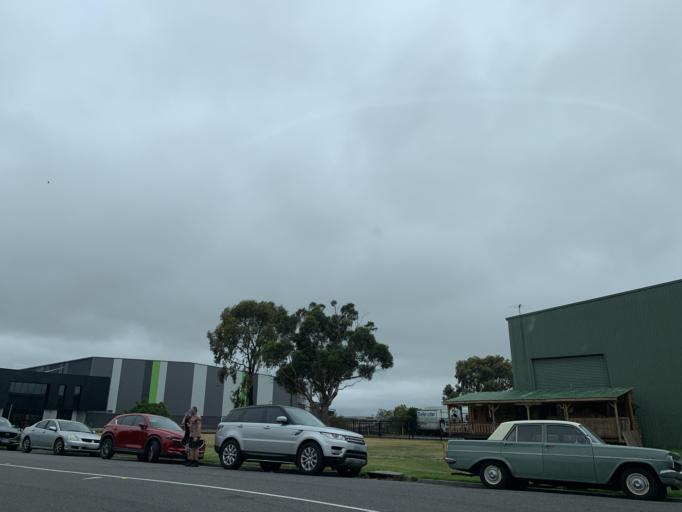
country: AU
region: Victoria
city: Heatherton
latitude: -37.9762
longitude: 145.0862
